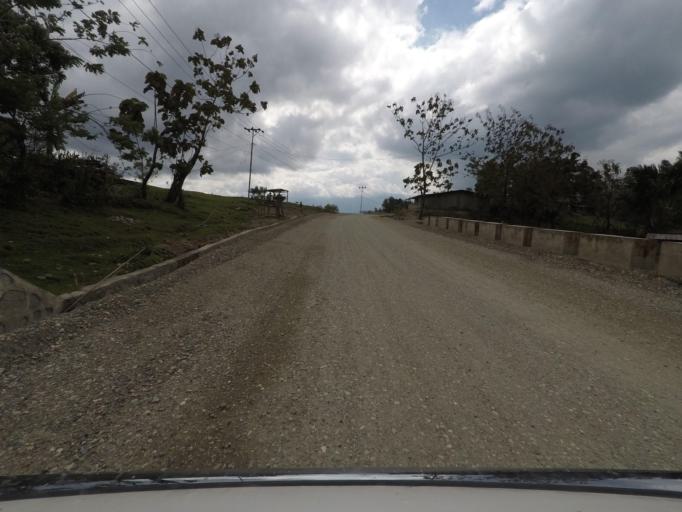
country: TL
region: Viqueque
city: Viqueque
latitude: -8.8010
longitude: 126.3778
